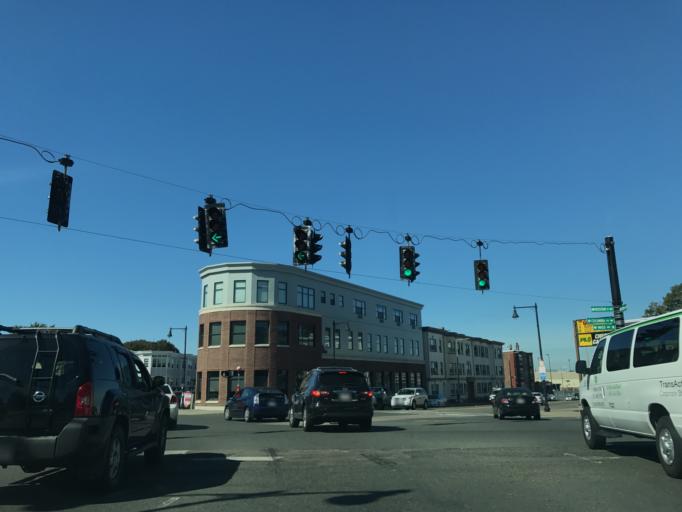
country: US
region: Massachusetts
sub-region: Suffolk County
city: South Boston
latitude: 42.3204
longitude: -71.0612
